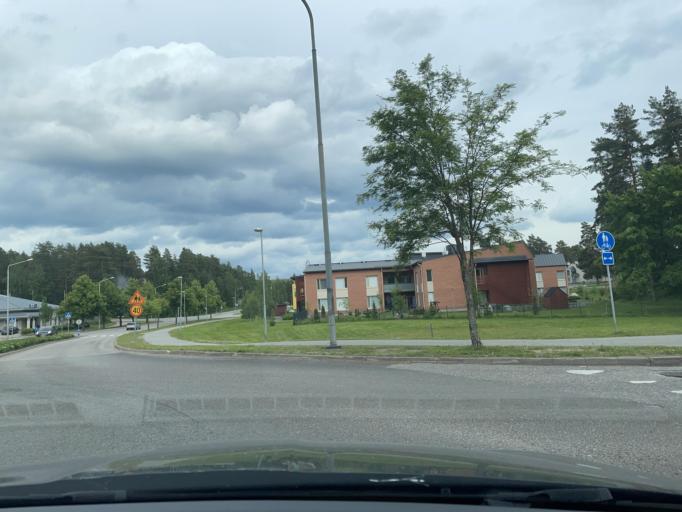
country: FI
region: Central Finland
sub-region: Jaemsae
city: Jaemsaenkoski
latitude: 61.9231
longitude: 25.1674
